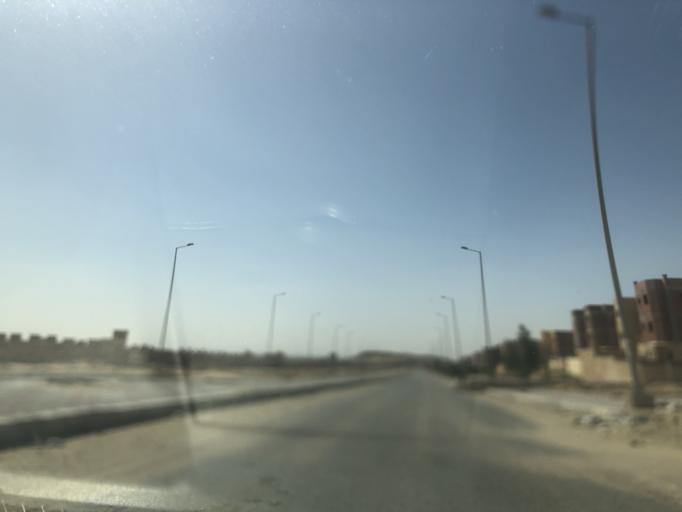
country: EG
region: Al Jizah
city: Madinat Sittah Uktubar
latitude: 29.9314
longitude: 30.9635
